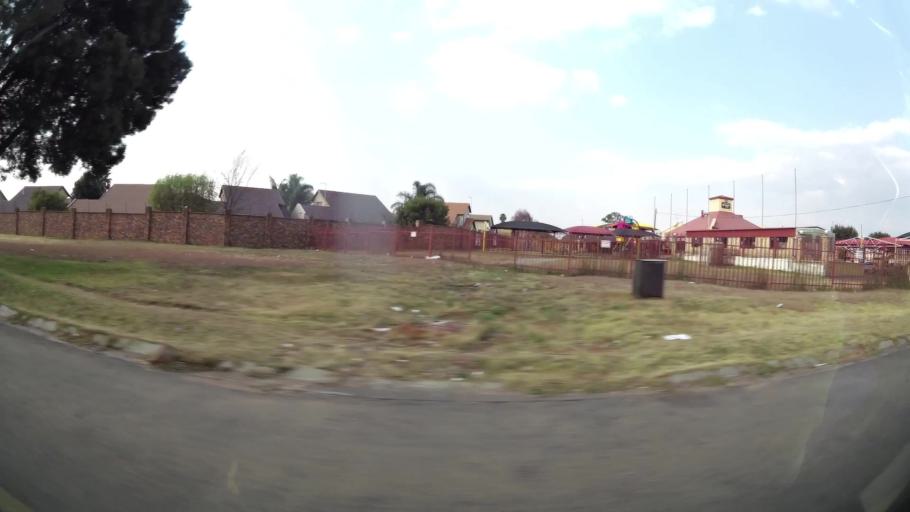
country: ZA
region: Gauteng
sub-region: Ekurhuleni Metropolitan Municipality
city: Benoni
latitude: -26.1438
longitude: 28.2972
